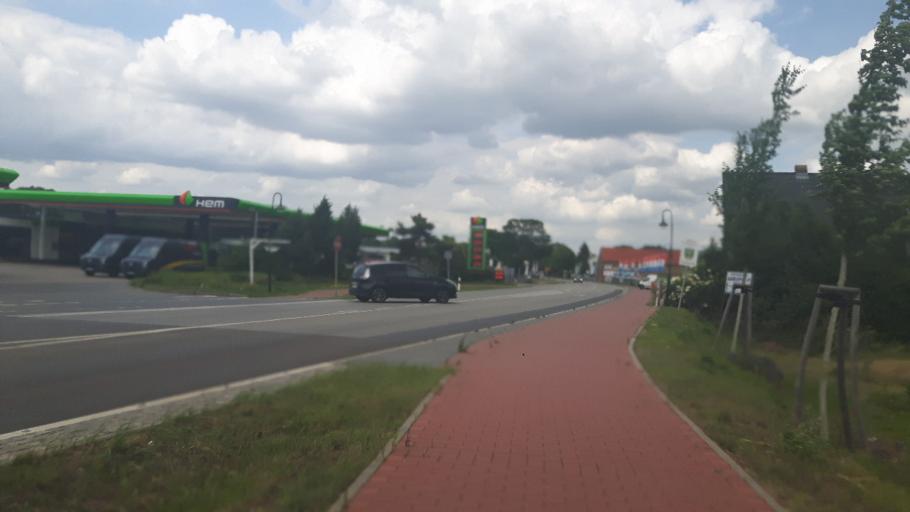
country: DE
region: Berlin
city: Buch
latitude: 52.6203
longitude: 13.5426
